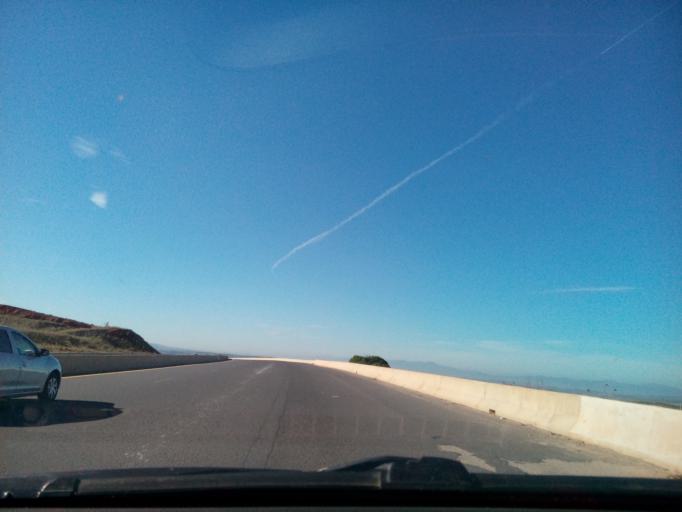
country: DZ
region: Tlemcen
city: Sidi Abdelli
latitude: 35.0198
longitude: -1.1437
